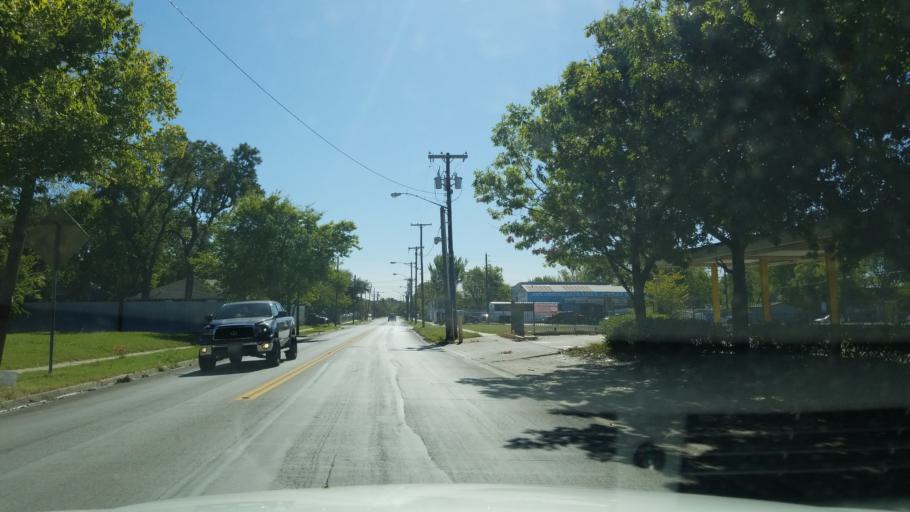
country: US
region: Texas
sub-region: Dallas County
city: Dallas
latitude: 32.7882
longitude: -96.7636
